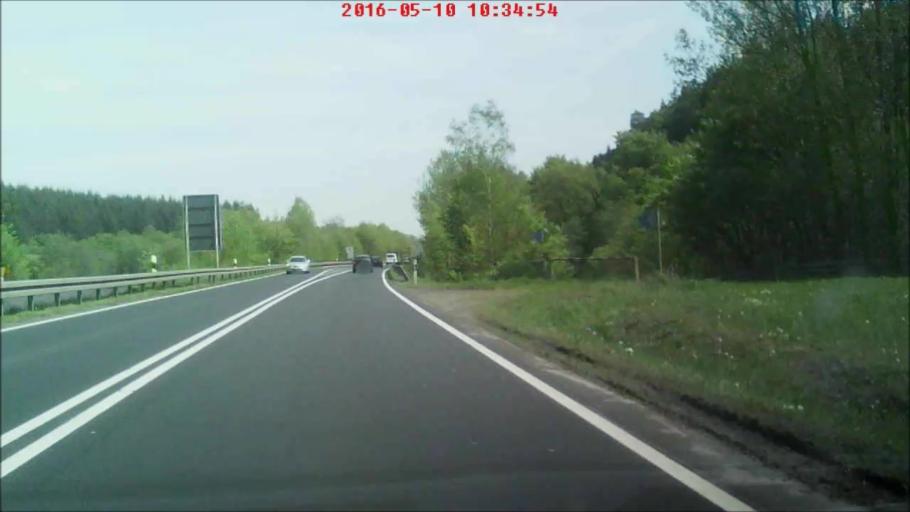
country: DE
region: Hesse
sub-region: Regierungsbezirk Kassel
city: Hunfeld
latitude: 50.6268
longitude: 9.7319
